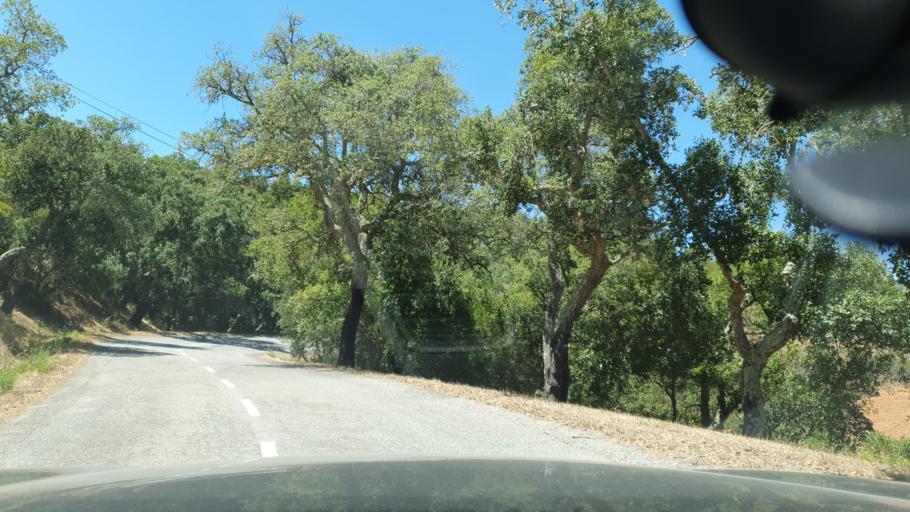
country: PT
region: Beja
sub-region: Odemira
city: Odemira
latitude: 37.6073
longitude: -8.4994
